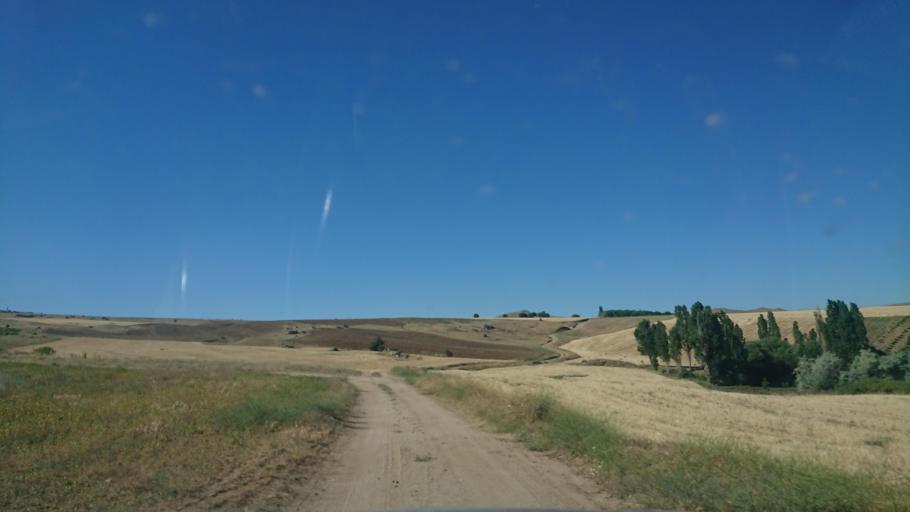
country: TR
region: Aksaray
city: Agacoren
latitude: 38.8510
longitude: 33.9394
